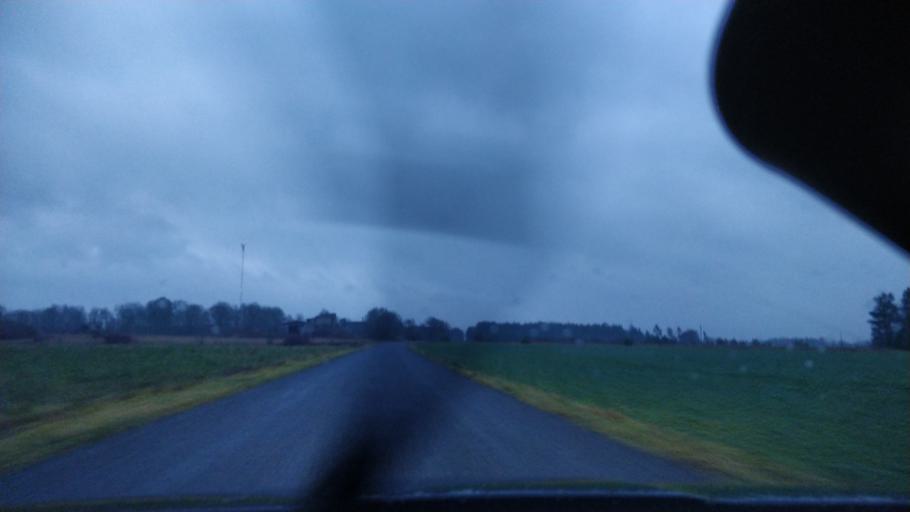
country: EE
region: Laeaene
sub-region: Lihula vald
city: Lihula
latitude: 58.8436
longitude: 24.0336
